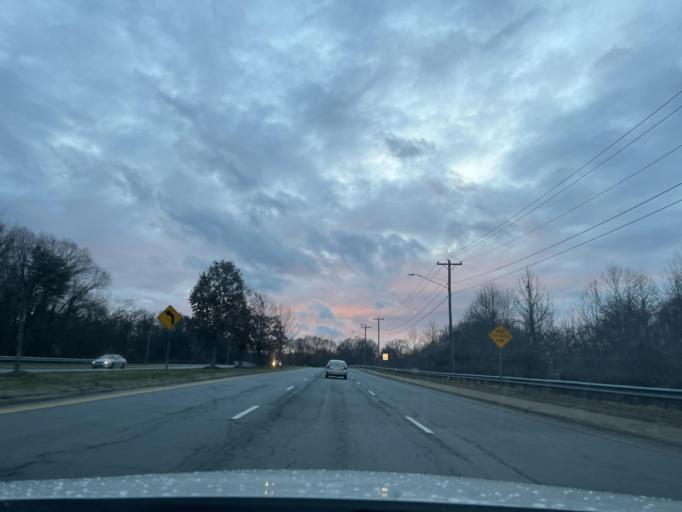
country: US
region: North Carolina
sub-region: Guilford County
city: Greensboro
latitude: 36.0478
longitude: -79.8478
